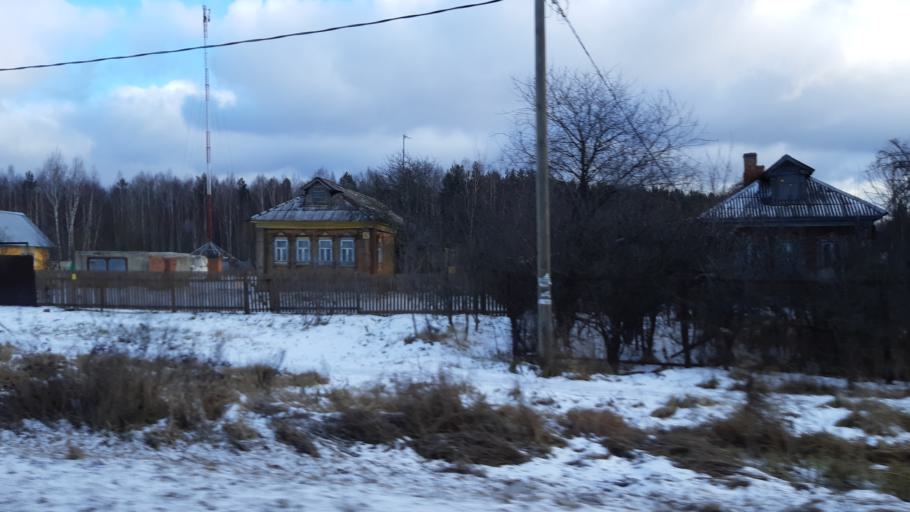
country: RU
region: Moskovskaya
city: Noginsk-9
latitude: 55.9973
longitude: 38.5446
